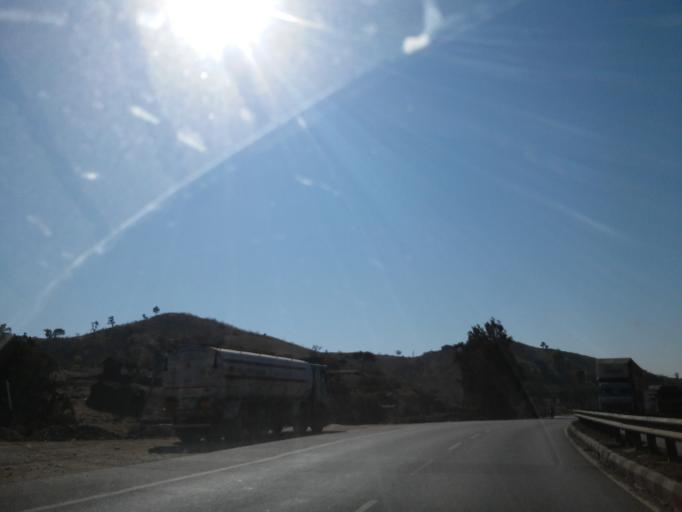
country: IN
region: Rajasthan
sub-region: Udaipur
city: Udaipur
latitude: 24.3773
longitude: 73.6362
